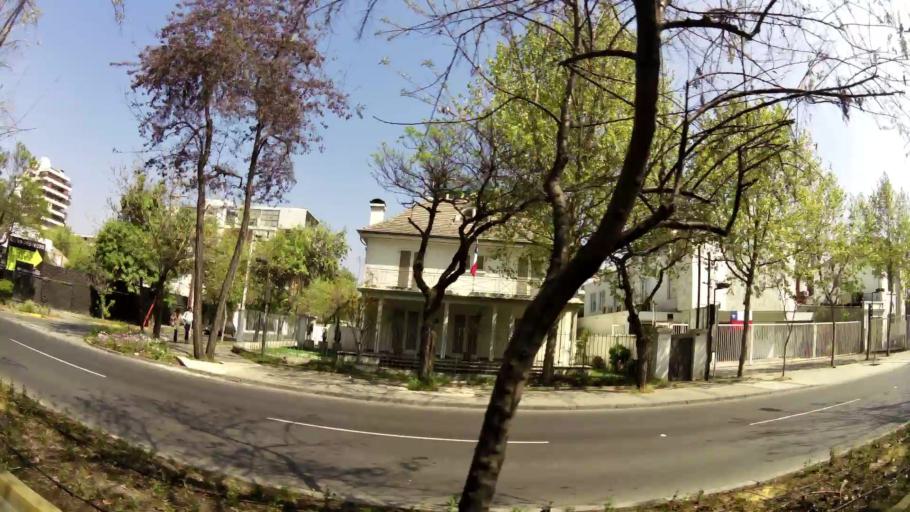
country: CL
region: Santiago Metropolitan
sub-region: Provincia de Santiago
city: Villa Presidente Frei, Nunoa, Santiago, Chile
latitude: -33.4242
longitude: -70.6043
